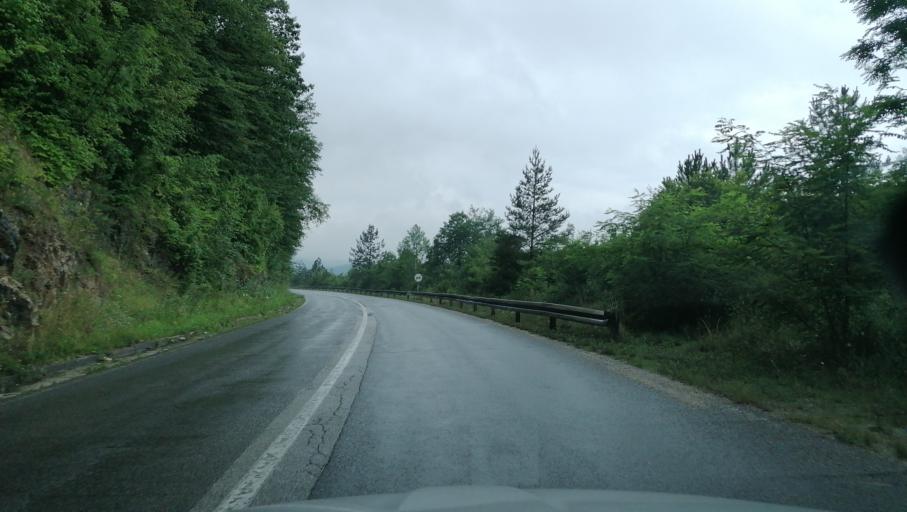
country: RS
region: Central Serbia
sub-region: Zlatiborski Okrug
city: Cajetina
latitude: 43.7905
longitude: 19.7098
